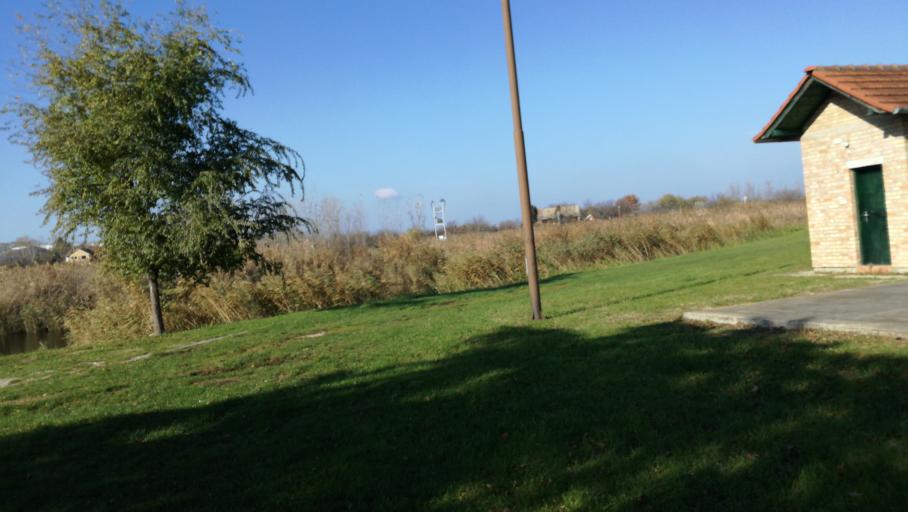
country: RS
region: Autonomna Pokrajina Vojvodina
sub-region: Severnobanatski Okrug
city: Kikinda
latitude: 45.8375
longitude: 20.4656
